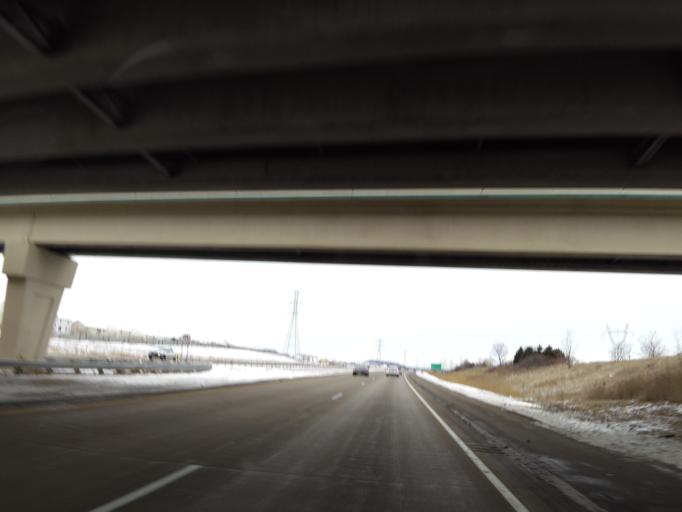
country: US
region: Minnesota
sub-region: Scott County
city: Shakopee
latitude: 44.7765
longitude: -93.5200
